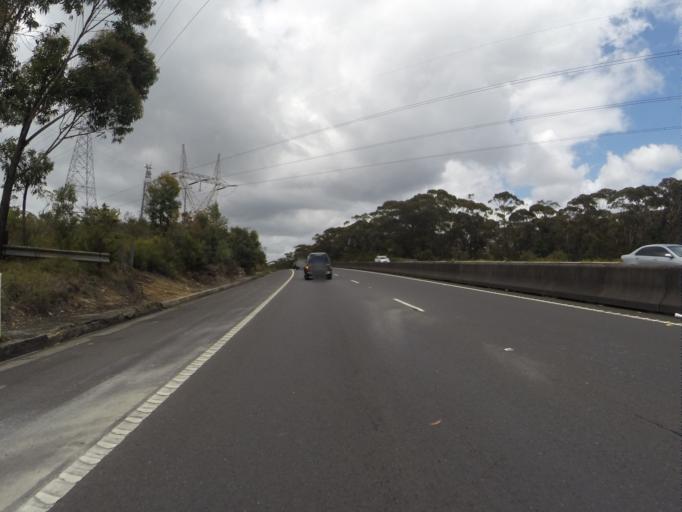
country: AU
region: New South Wales
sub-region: Wollongong
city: Bulli
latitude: -34.3222
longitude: 150.8840
